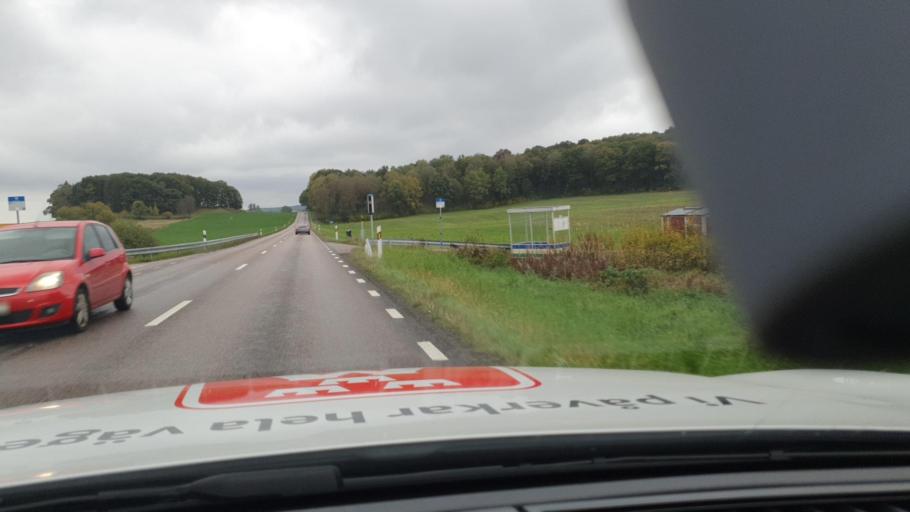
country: SE
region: Halland
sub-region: Falkenbergs Kommun
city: Falkenberg
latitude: 57.0394
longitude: 12.6020
